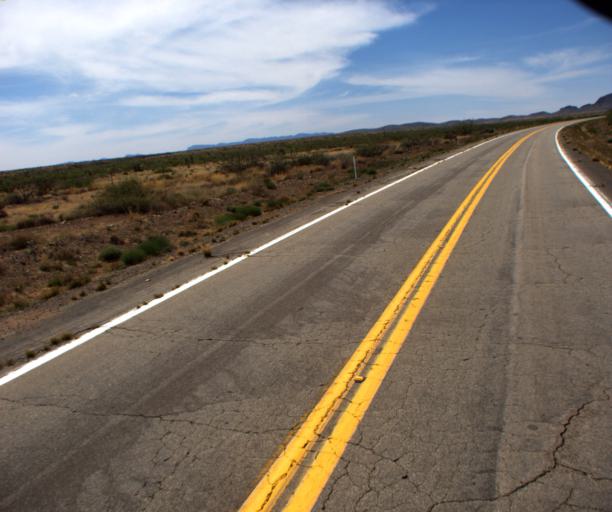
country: US
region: Arizona
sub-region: Cochise County
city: Willcox
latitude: 32.3734
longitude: -109.6382
